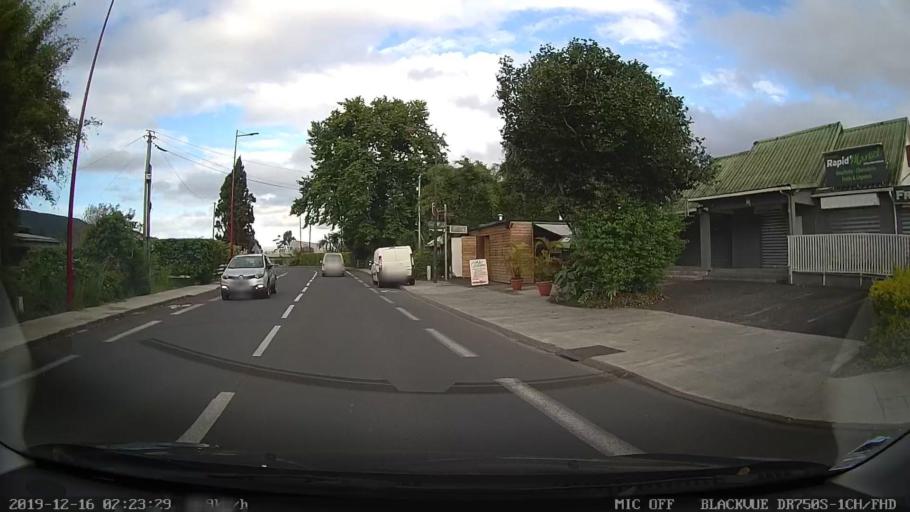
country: RE
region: Reunion
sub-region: Reunion
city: Salazie
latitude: -21.1427
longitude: 55.6212
